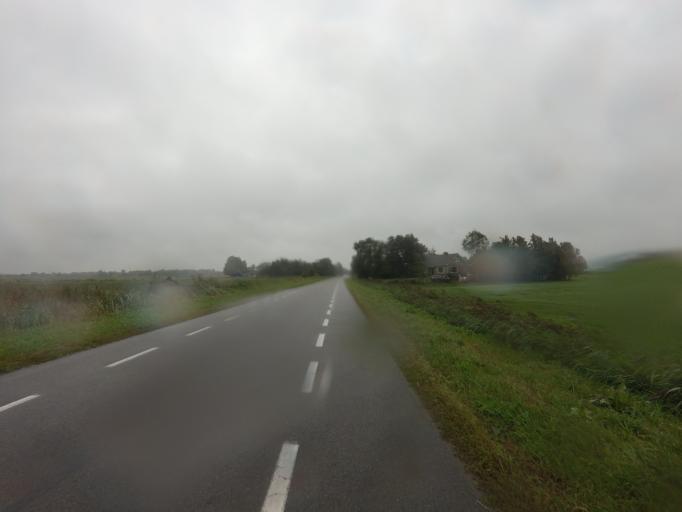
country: NL
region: Friesland
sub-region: Gemeente Smallingerland
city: Oudega
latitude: 53.0964
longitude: 5.9708
